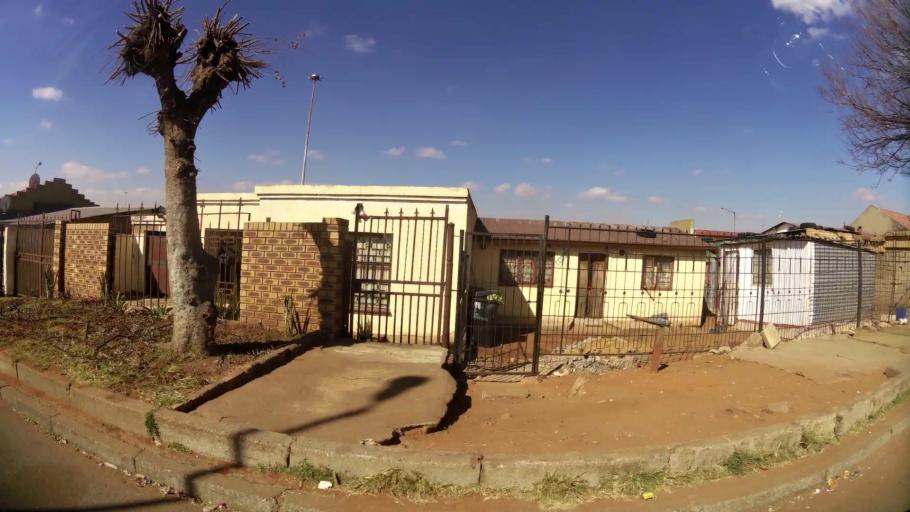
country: ZA
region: Gauteng
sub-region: City of Johannesburg Metropolitan Municipality
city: Soweto
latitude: -26.2233
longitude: 27.9115
